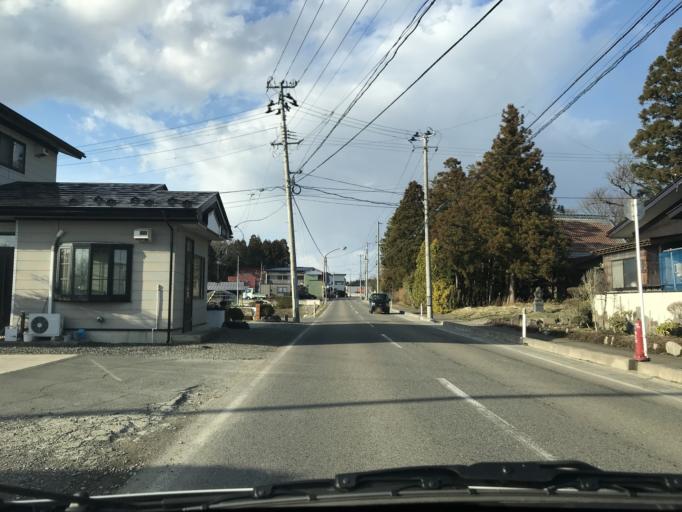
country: JP
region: Iwate
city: Kitakami
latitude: 39.3158
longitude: 141.0679
